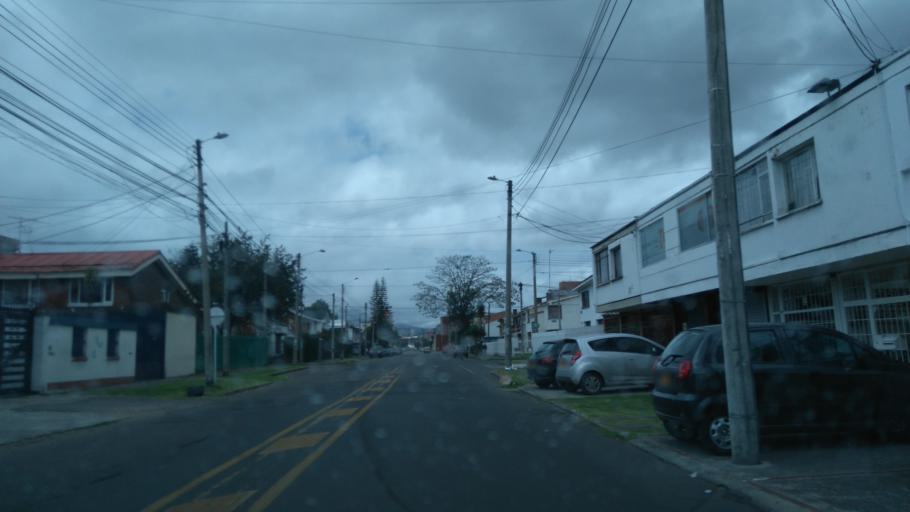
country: CO
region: Bogota D.C.
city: Barrio San Luis
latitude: 4.6729
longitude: -74.0614
